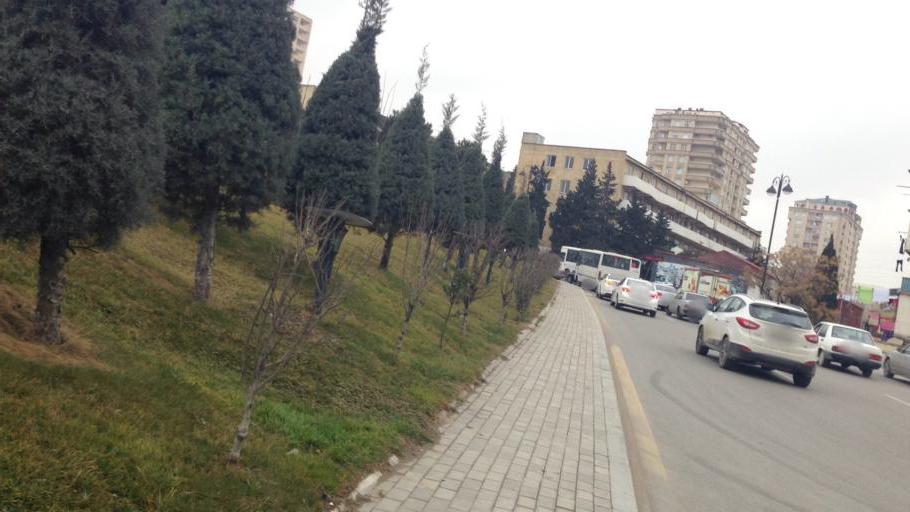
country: AZ
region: Baki
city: Badamdar
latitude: 40.3796
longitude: 49.8081
